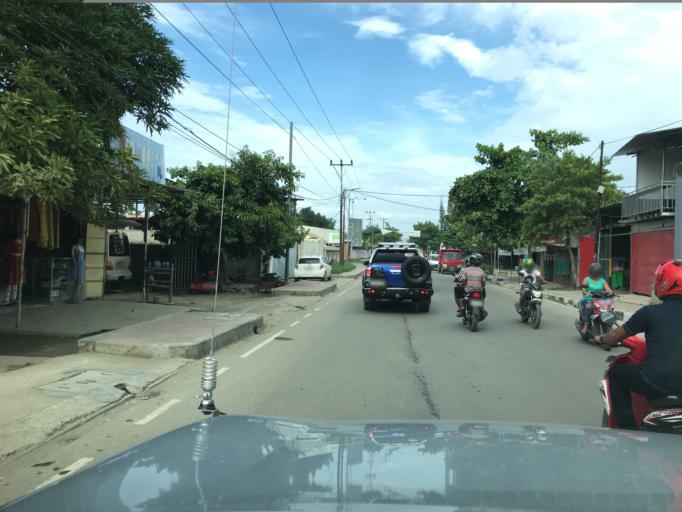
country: TL
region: Dili
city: Dili
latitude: -8.5599
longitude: 125.5635
